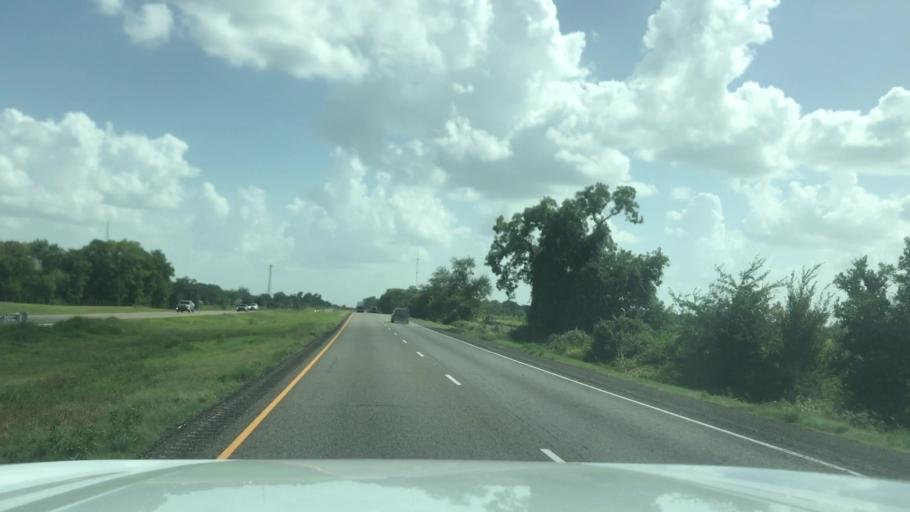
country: US
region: Texas
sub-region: Grimes County
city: Navasota
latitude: 30.2665
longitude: -96.0415
